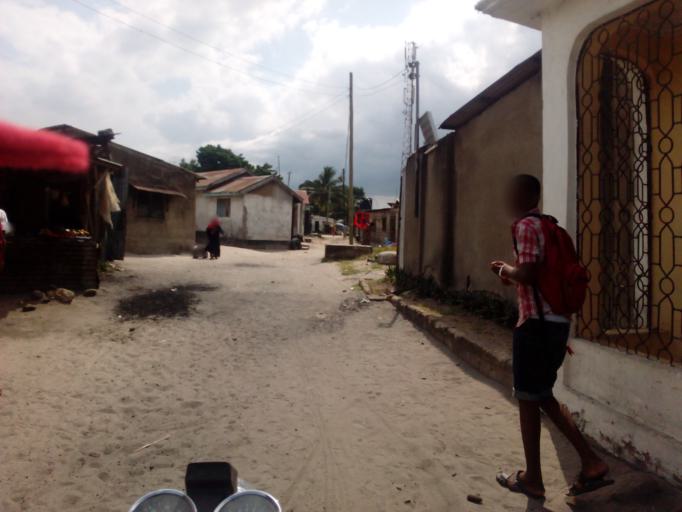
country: TZ
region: Dar es Salaam
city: Dar es Salaam
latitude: -6.8574
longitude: 39.2555
